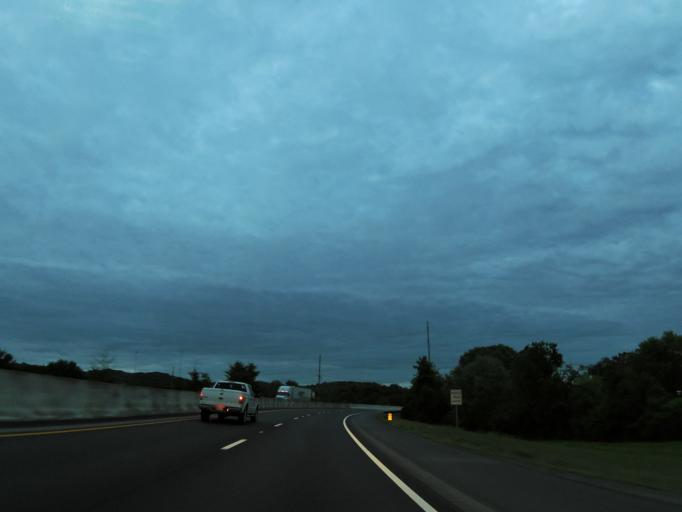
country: US
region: Tennessee
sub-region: Davidson County
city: Nashville
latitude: 36.2317
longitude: -86.8272
